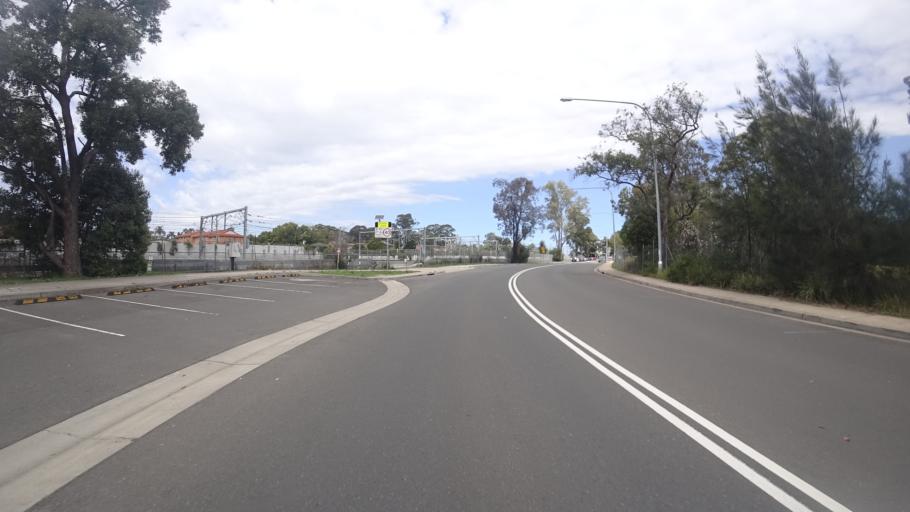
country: AU
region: New South Wales
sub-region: Campbelltown Municipality
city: Glenfield
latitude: -33.9680
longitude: 150.8967
